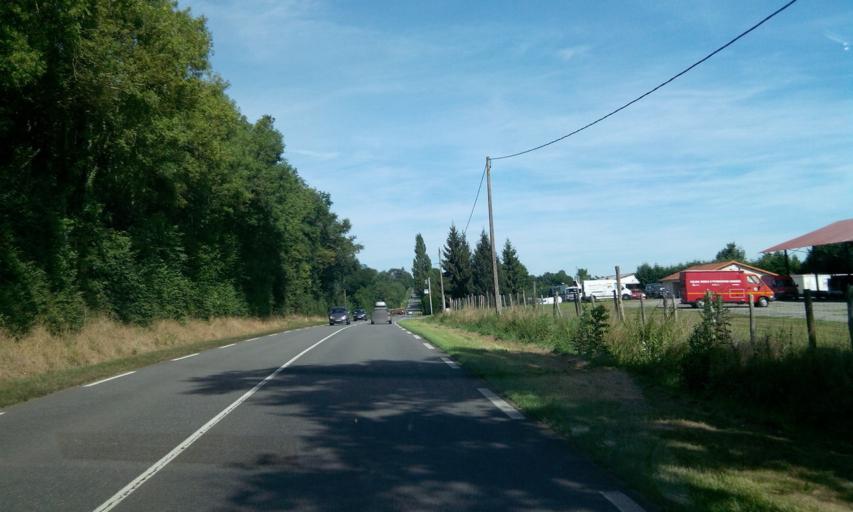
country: FR
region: Poitou-Charentes
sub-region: Departement de la Charente
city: Confolens
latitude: 45.9702
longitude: 0.6924
